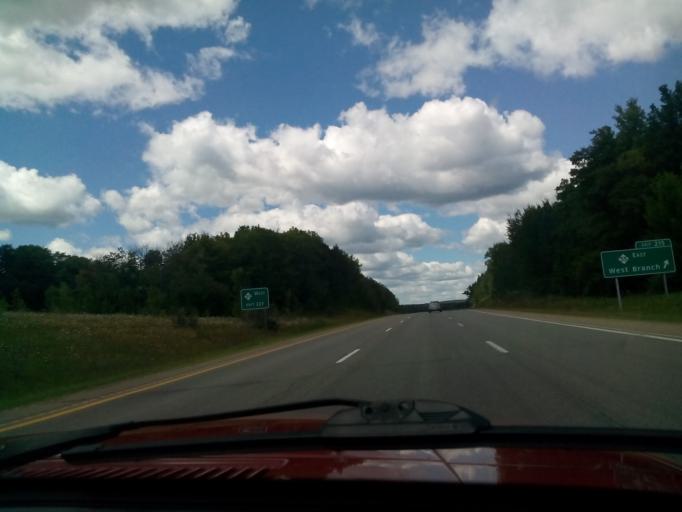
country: US
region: Michigan
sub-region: Ogemaw County
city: West Branch
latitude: 44.2688
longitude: -84.2727
